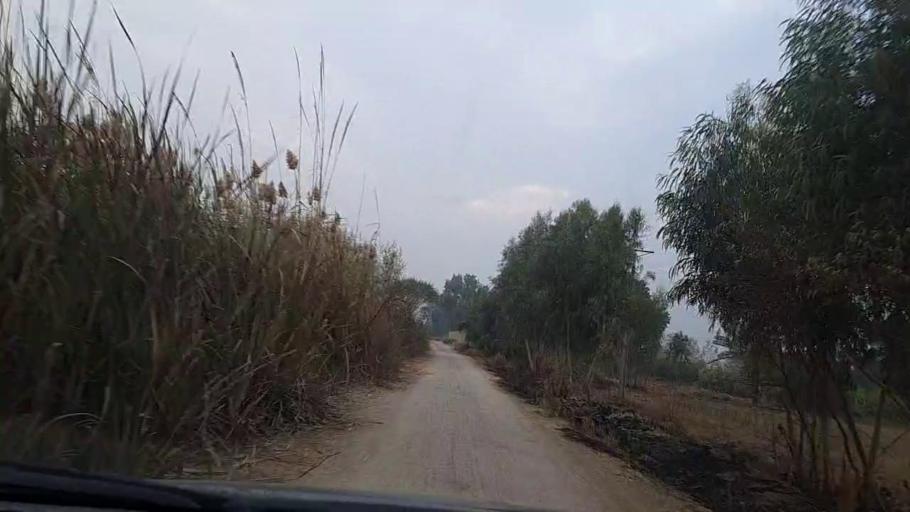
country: PK
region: Sindh
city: Sakrand
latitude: 26.2892
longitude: 68.2454
